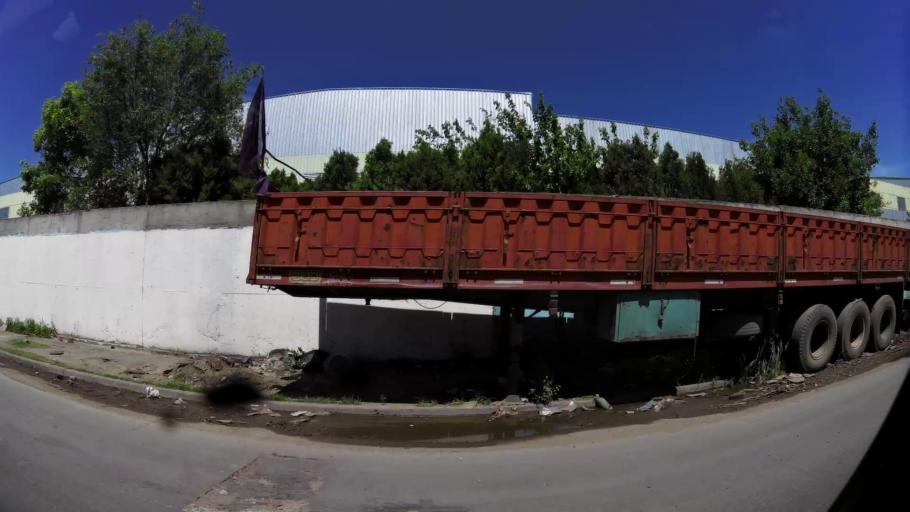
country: AR
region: Buenos Aires
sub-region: Partido de Lanus
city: Lanus
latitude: -34.7343
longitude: -58.3414
